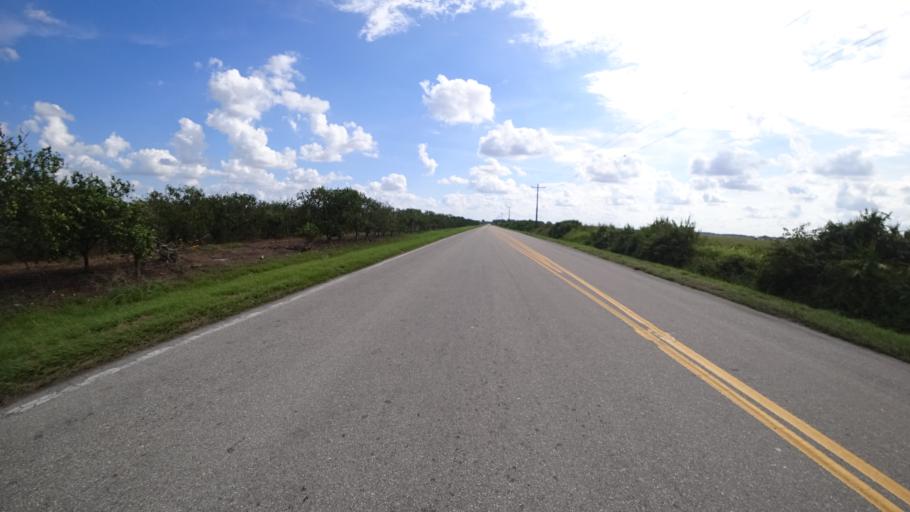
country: US
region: Florida
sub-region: Hillsborough County
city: Wimauma
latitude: 27.5884
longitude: -82.1037
